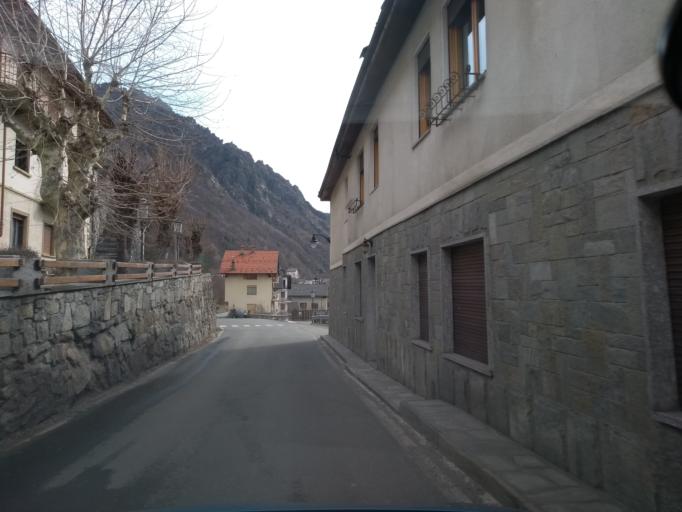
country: IT
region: Piedmont
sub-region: Provincia di Torino
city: Chialamberto
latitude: 45.3629
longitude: 7.3445
